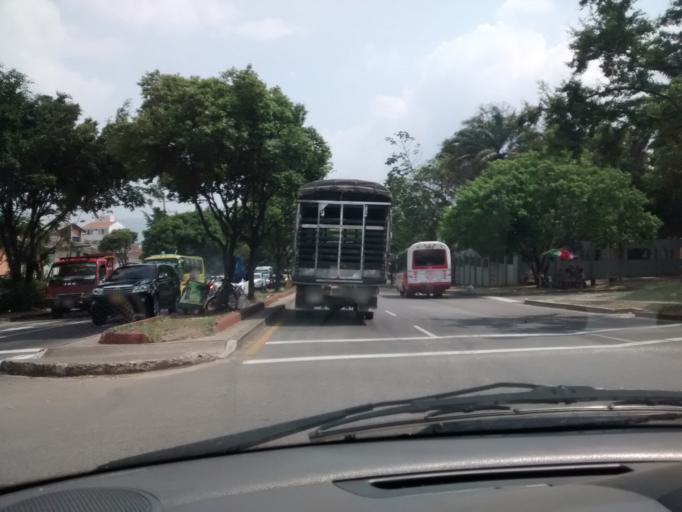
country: CO
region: Santander
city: Bucaramanga
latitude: 7.1023
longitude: -73.1134
